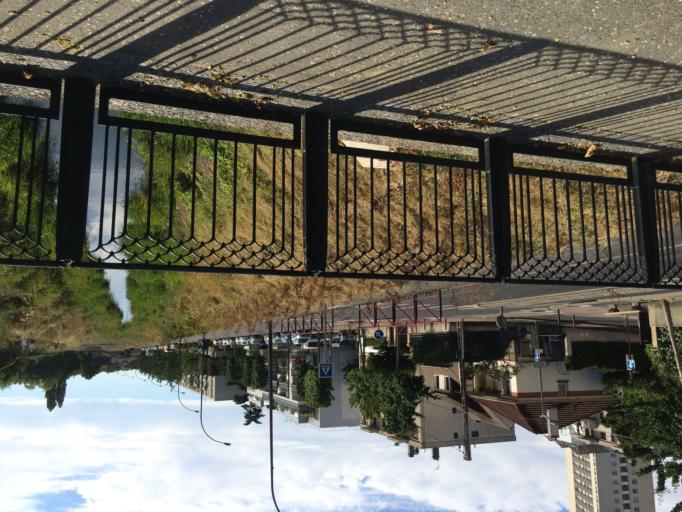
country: FR
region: Ile-de-France
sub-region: Departement des Hauts-de-Seine
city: Bourg-la-Reine
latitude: 48.7698
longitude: 2.3218
